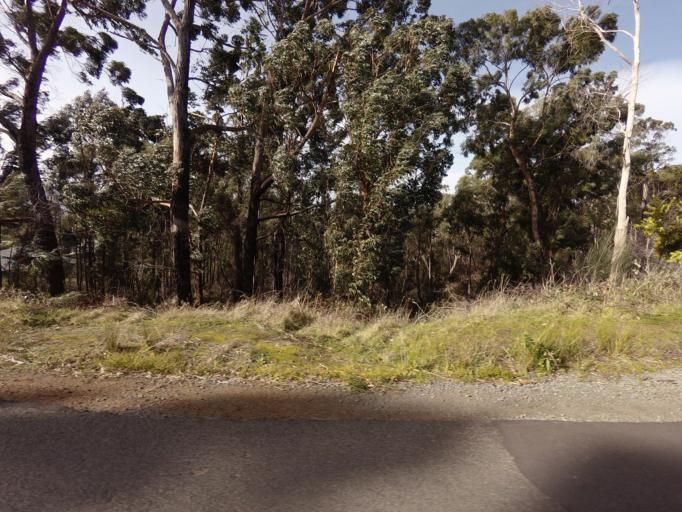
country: AU
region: Tasmania
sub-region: Kingborough
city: Margate
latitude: -43.0769
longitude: 147.2654
